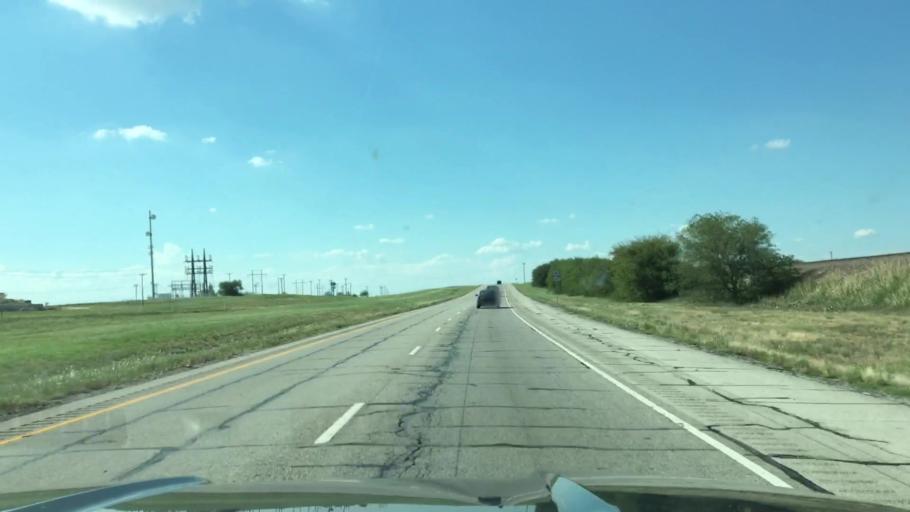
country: US
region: Texas
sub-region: Wise County
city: Decatur
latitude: 33.1761
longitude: -97.5436
